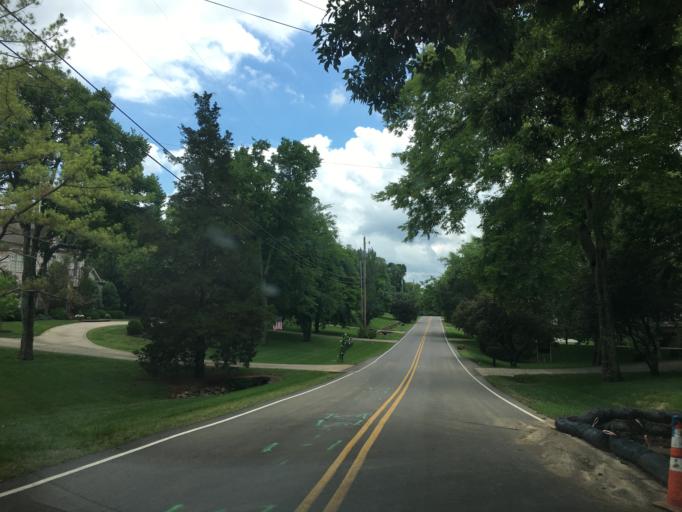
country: US
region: Tennessee
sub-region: Davidson County
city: Forest Hills
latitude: 36.0853
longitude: -86.8418
